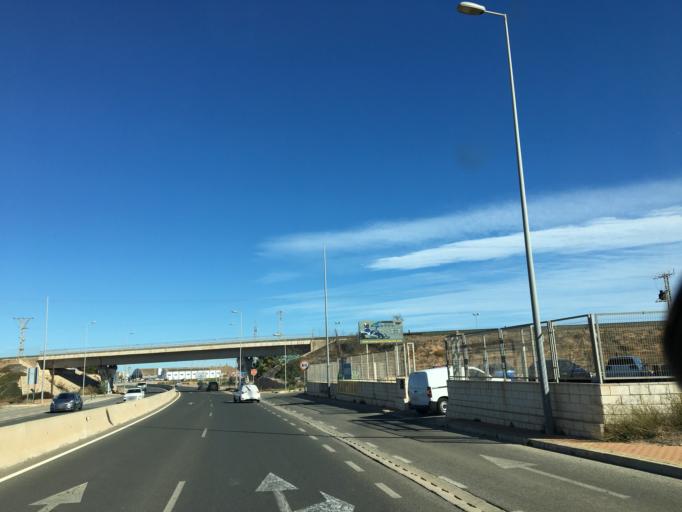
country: ES
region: Murcia
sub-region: Murcia
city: Cartagena
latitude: 37.6408
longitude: -0.9869
